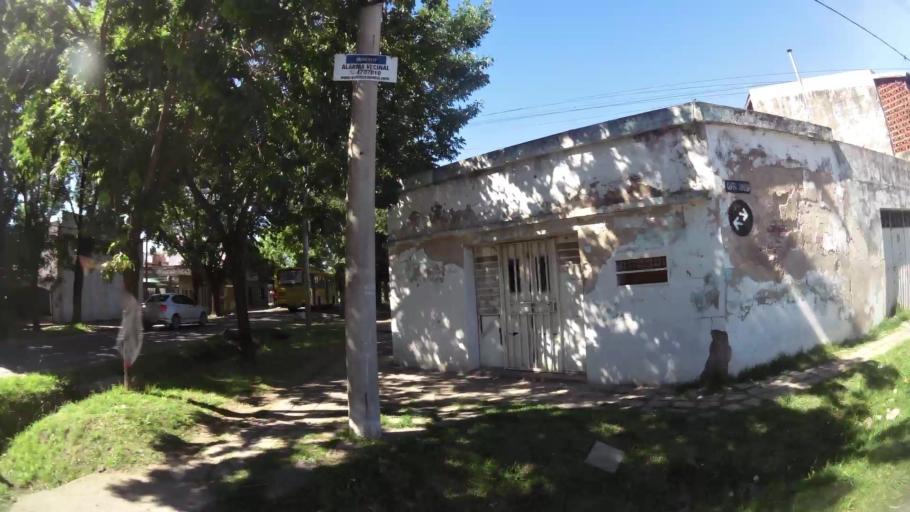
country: AR
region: Santa Fe
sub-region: Departamento de Rosario
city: Rosario
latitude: -32.9606
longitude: -60.6940
